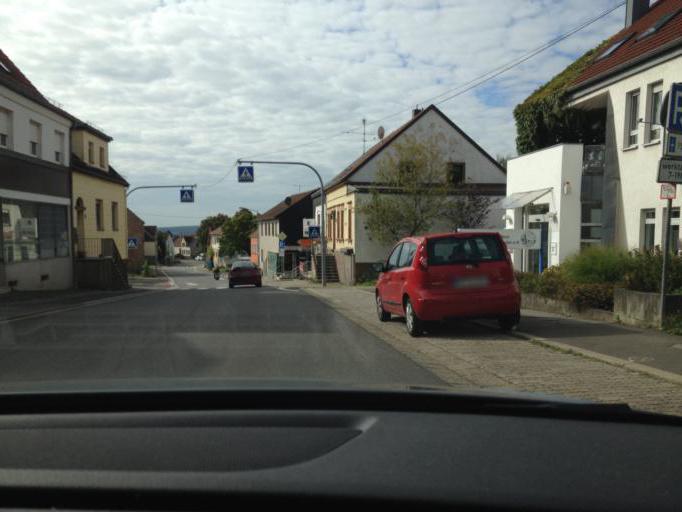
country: DE
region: Saarland
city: Mainzweiler
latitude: 49.3901
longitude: 7.1136
